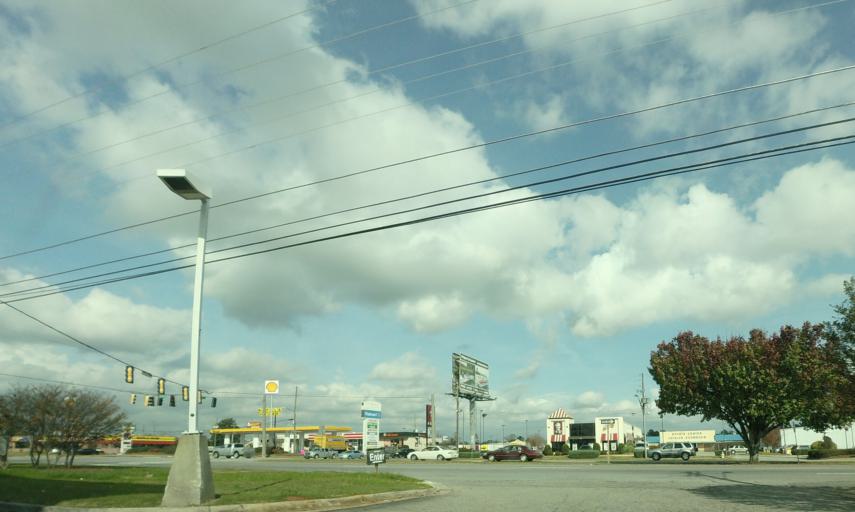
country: US
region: Georgia
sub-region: Houston County
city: Perry
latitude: 32.4692
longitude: -83.7419
